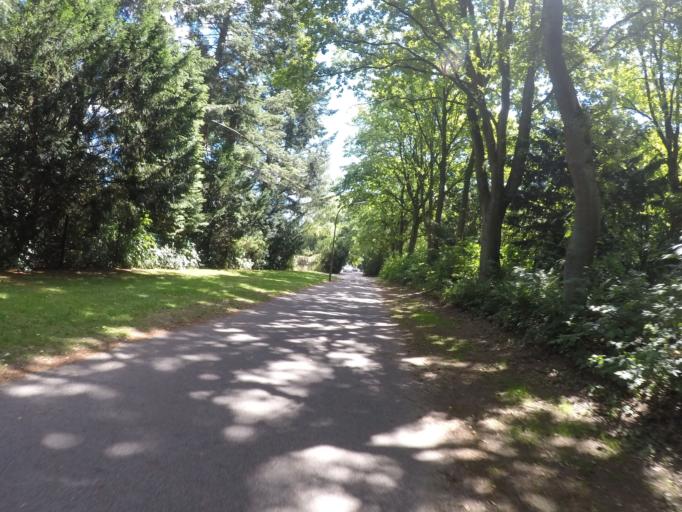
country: DE
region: Schleswig-Holstein
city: Halstenbek
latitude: 53.5737
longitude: 9.8004
